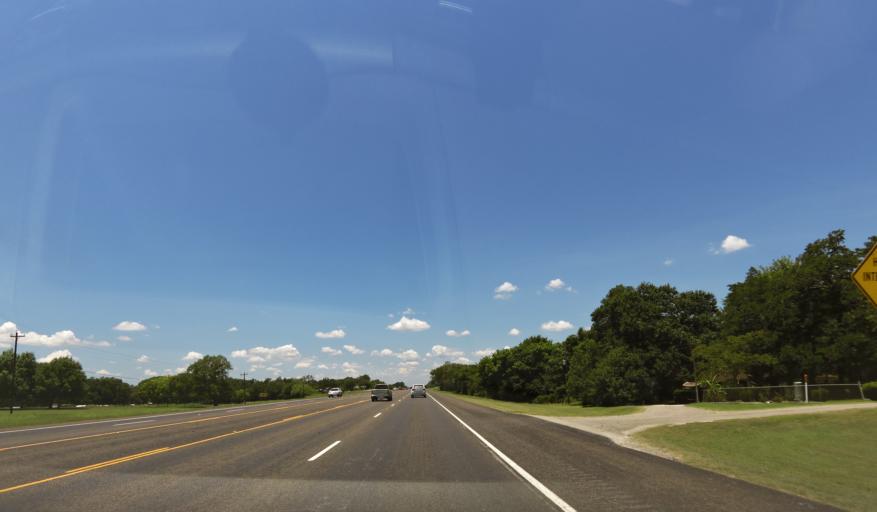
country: US
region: Texas
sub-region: Washington County
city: Brenham
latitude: 30.1780
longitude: -96.4674
